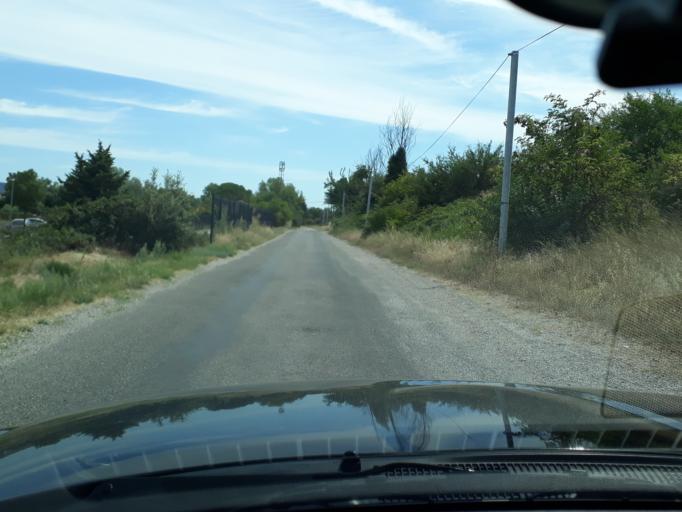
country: FR
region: Provence-Alpes-Cote d'Azur
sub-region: Departement du Vaucluse
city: Carpentras
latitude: 44.0397
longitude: 5.0462
